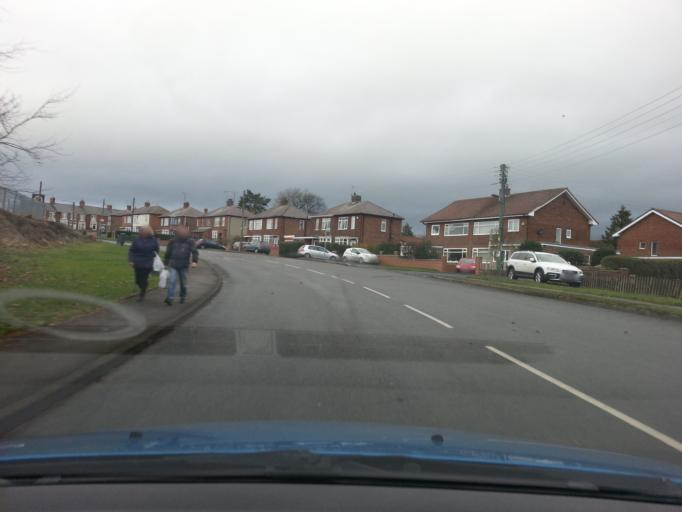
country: GB
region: England
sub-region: County Durham
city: Crook
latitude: 54.7074
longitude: -1.7479
